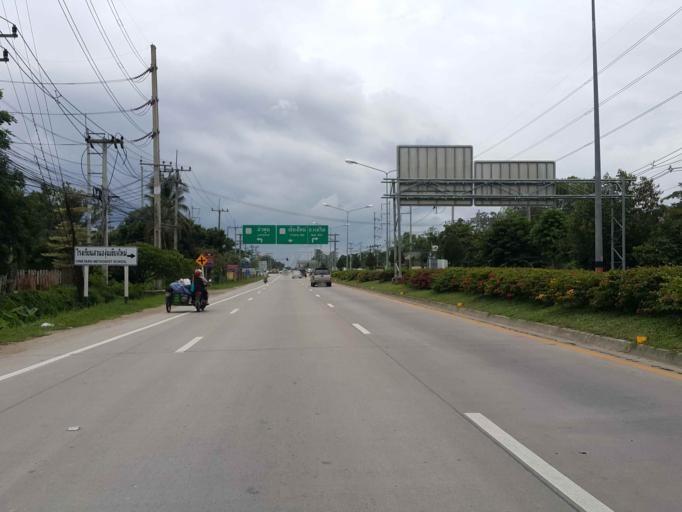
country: TH
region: Chiang Mai
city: San Sai
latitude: 18.8281
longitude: 99.0501
